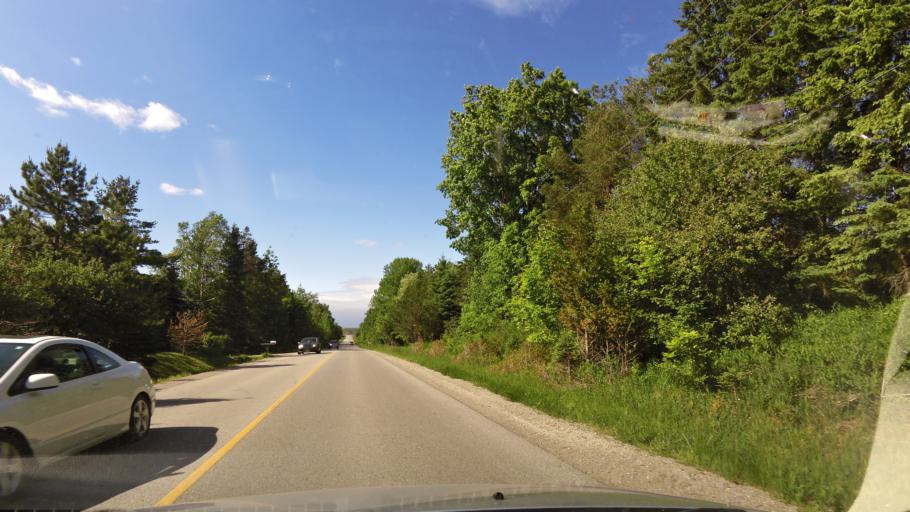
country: CA
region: Ontario
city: Bradford West Gwillimbury
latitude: 44.1975
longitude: -79.6245
